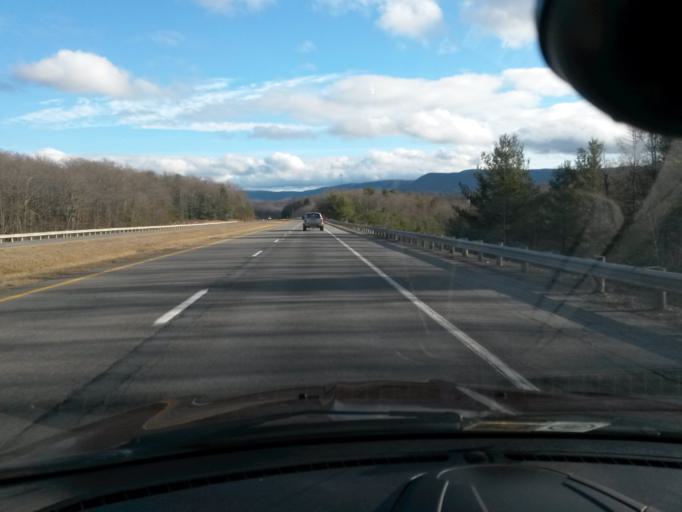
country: US
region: West Virginia
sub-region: Mercer County
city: Athens
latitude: 37.3597
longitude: -81.0271
